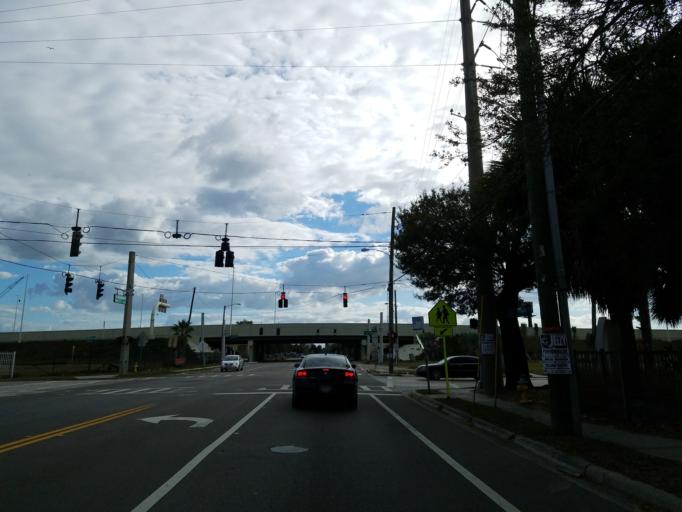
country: US
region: Florida
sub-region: Hillsborough County
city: Tampa
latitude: 27.9573
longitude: -82.4685
